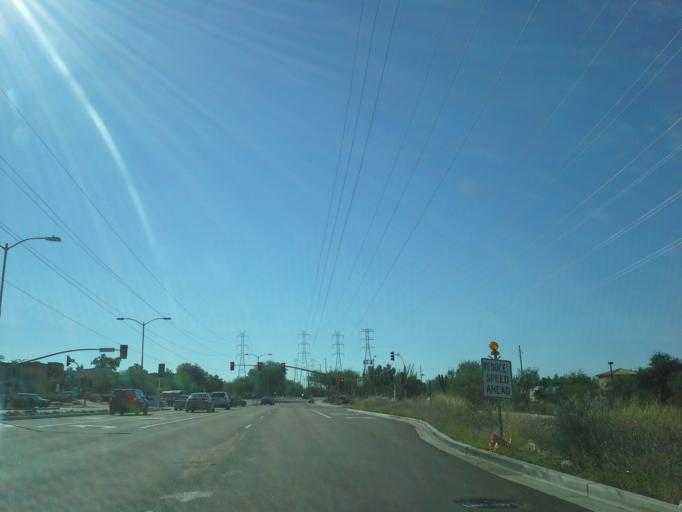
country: US
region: Arizona
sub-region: Maricopa County
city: Scottsdale
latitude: 33.5899
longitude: -111.8369
